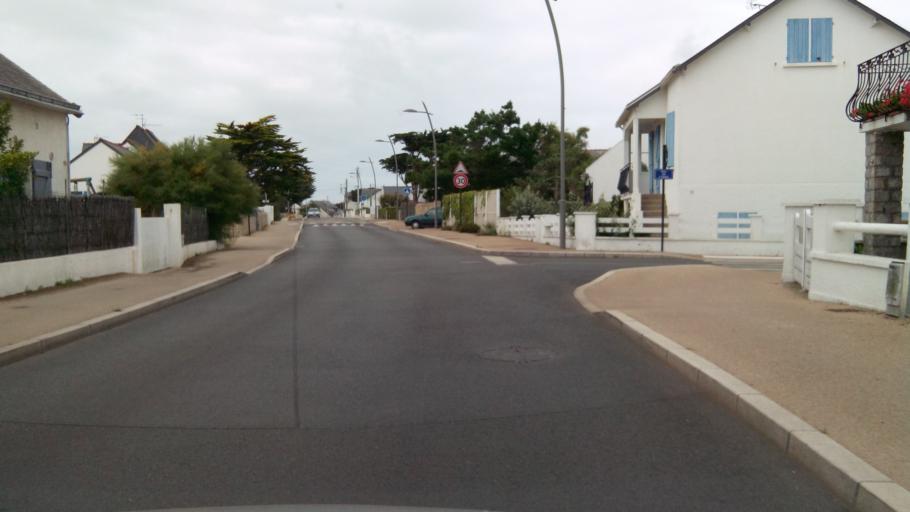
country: FR
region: Pays de la Loire
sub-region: Departement de la Loire-Atlantique
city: Batz-sur-Mer
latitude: 47.2760
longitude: -2.4877
